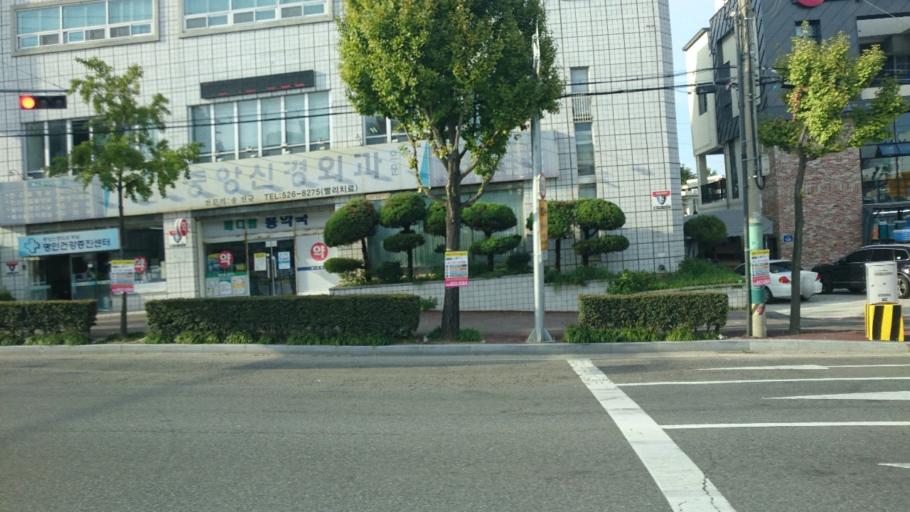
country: KR
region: Gwangju
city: Gwangju
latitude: 35.1527
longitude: 126.8974
